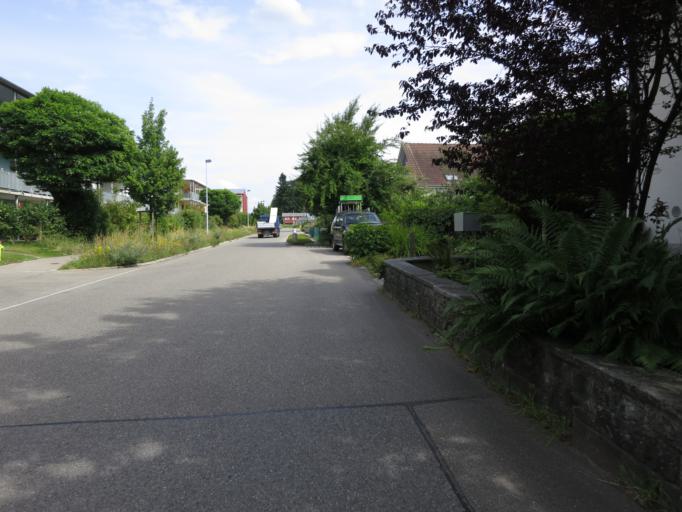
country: CH
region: Zurich
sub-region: Bezirk Hinwil
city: Wolfhausen
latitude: 47.2543
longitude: 8.8032
